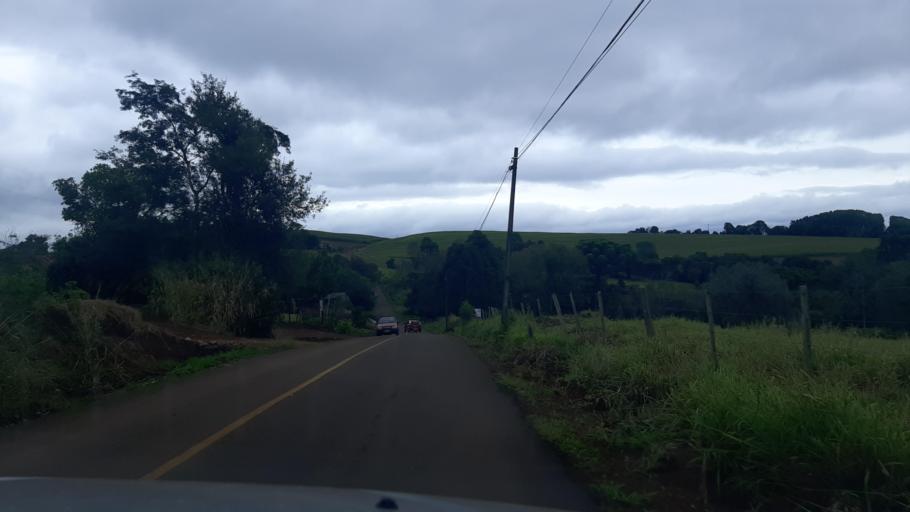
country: BR
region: Parana
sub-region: Ampere
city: Ampere
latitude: -26.0377
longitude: -53.4893
